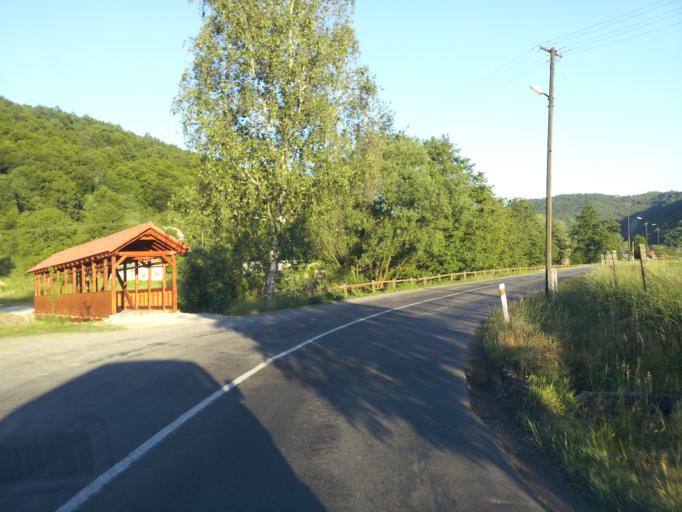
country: SK
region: Banskobystricky
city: Svaety Anton
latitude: 48.3558
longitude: 18.9259
